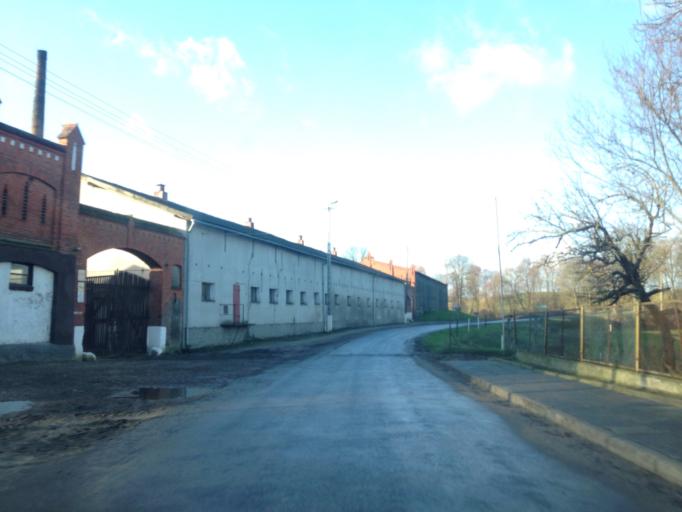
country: PL
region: Kujawsko-Pomorskie
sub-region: Powiat grudziadzki
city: Swiecie nad Osa
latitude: 53.4707
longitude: 19.1084
